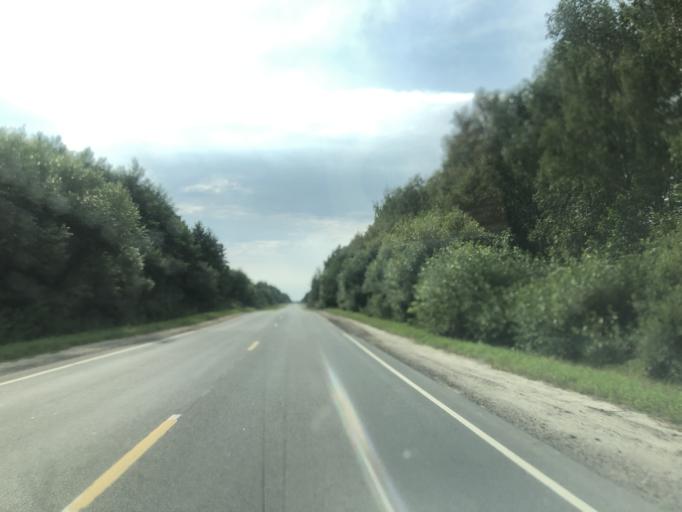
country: RU
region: Ivanovo
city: Shuya
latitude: 56.8561
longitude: 41.5361
